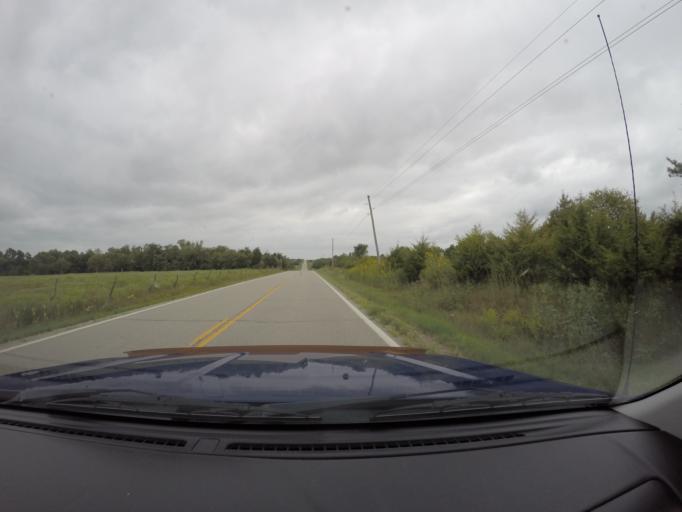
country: US
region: Kansas
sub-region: Morris County
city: Council Grove
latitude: 38.8133
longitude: -96.5942
